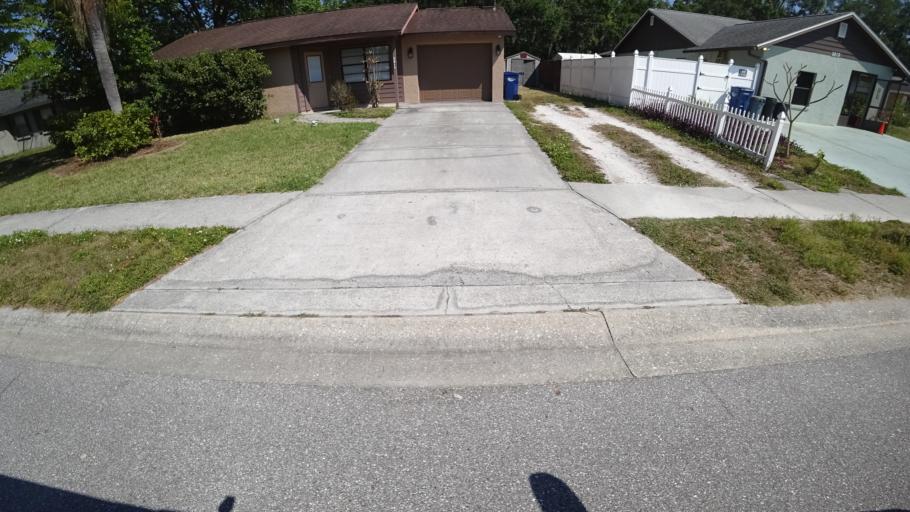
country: US
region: Florida
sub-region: Manatee County
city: Samoset
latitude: 27.4689
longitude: -82.5282
